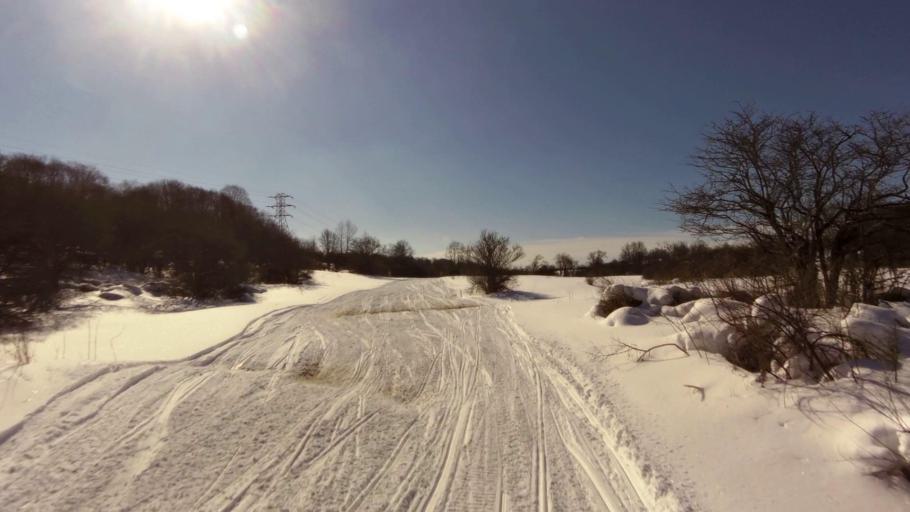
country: US
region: New York
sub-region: Cattaraugus County
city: Franklinville
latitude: 42.3998
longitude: -78.4962
